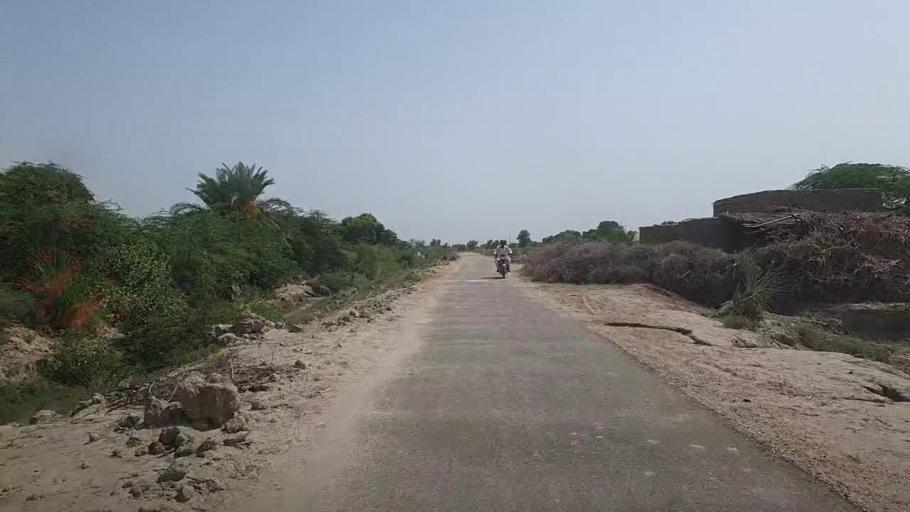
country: PK
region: Sindh
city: Pad Idan
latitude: 26.8289
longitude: 68.3300
